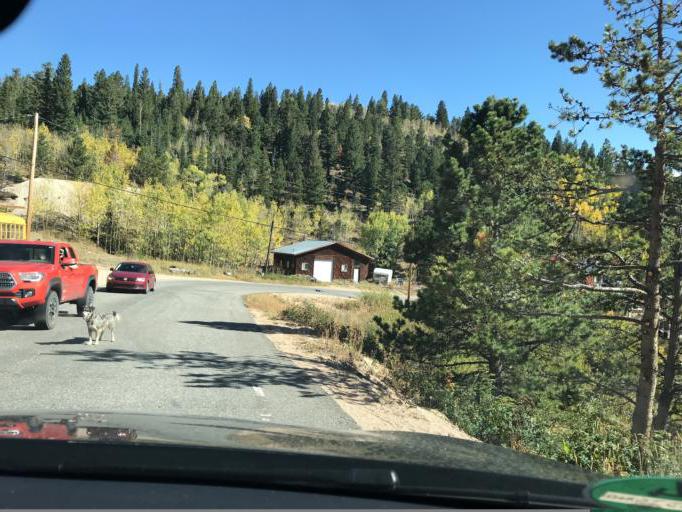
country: US
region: Colorado
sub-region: Boulder County
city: Nederland
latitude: 40.0742
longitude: -105.5068
